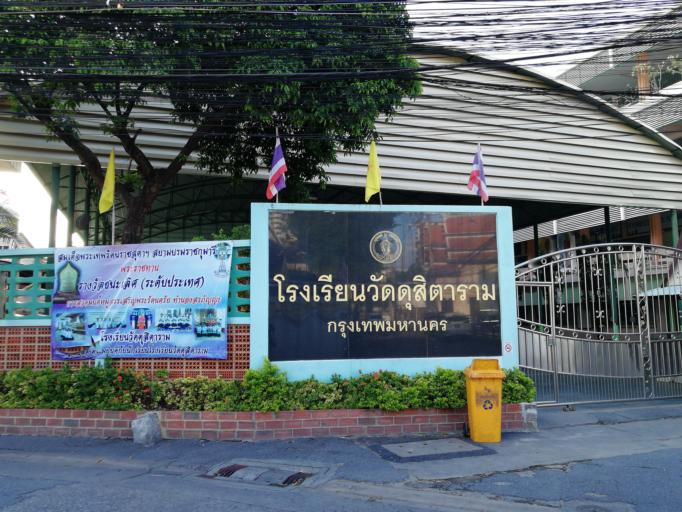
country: TH
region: Bangkok
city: Bangkok Noi
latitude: 13.7640
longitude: 100.4874
